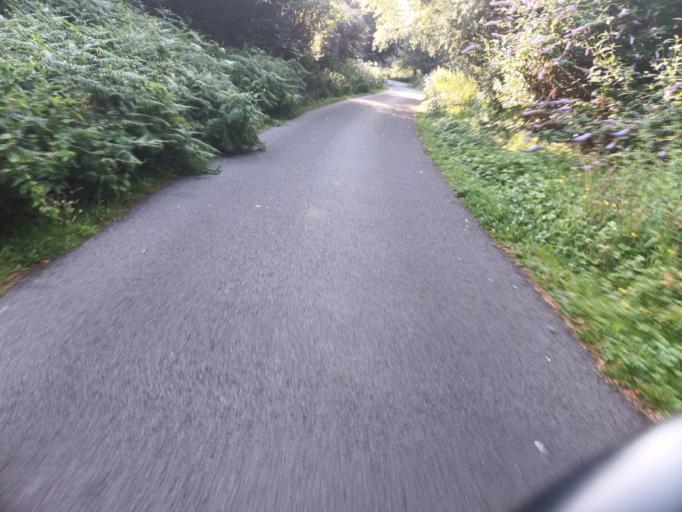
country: GB
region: Northern Ireland
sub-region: Castlereagh District
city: Dundonald
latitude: 54.5886
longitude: -5.8078
